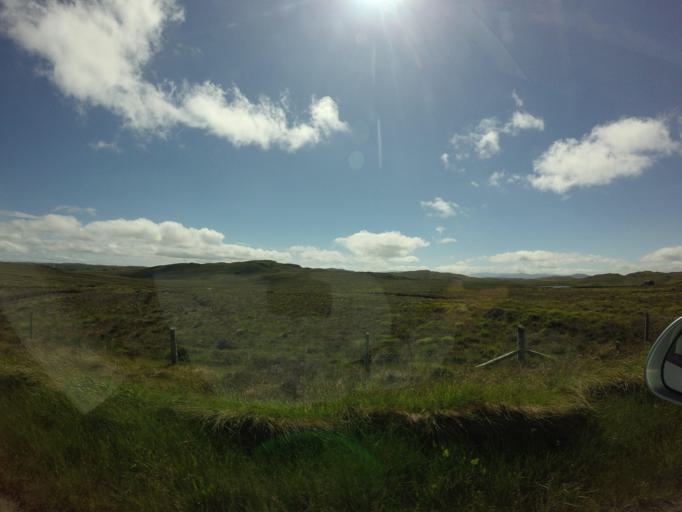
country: GB
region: Scotland
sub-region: Eilean Siar
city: Stornoway
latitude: 58.1577
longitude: -6.5187
